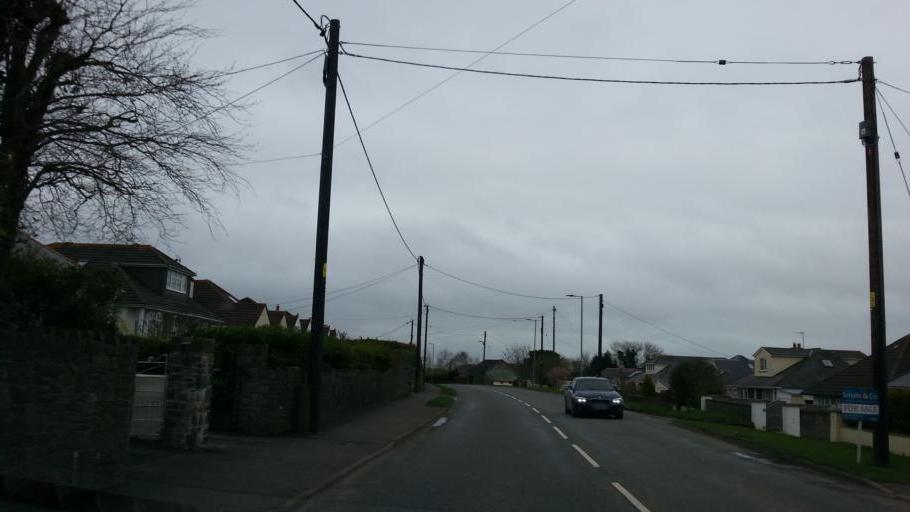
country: GB
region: England
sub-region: Devon
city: Fremington
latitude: 51.0697
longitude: -4.1493
